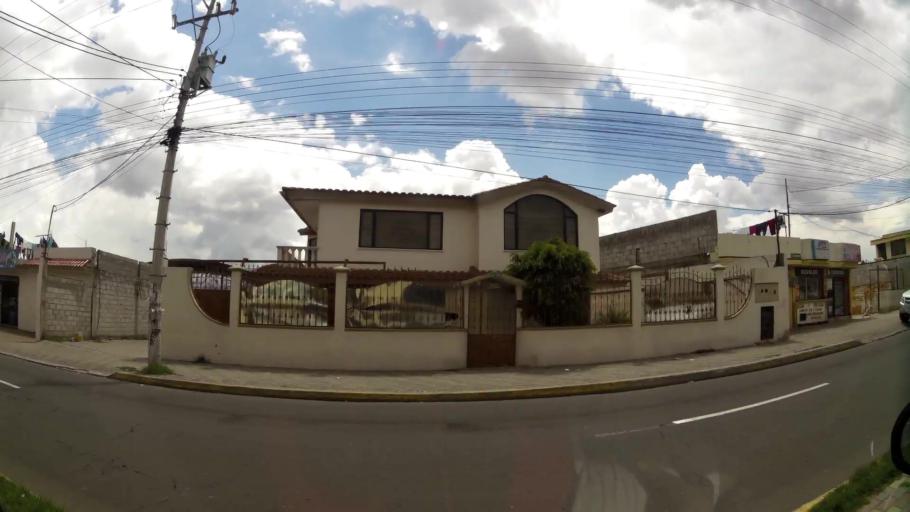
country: EC
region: Pichincha
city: Quito
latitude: -0.0971
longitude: -78.4416
